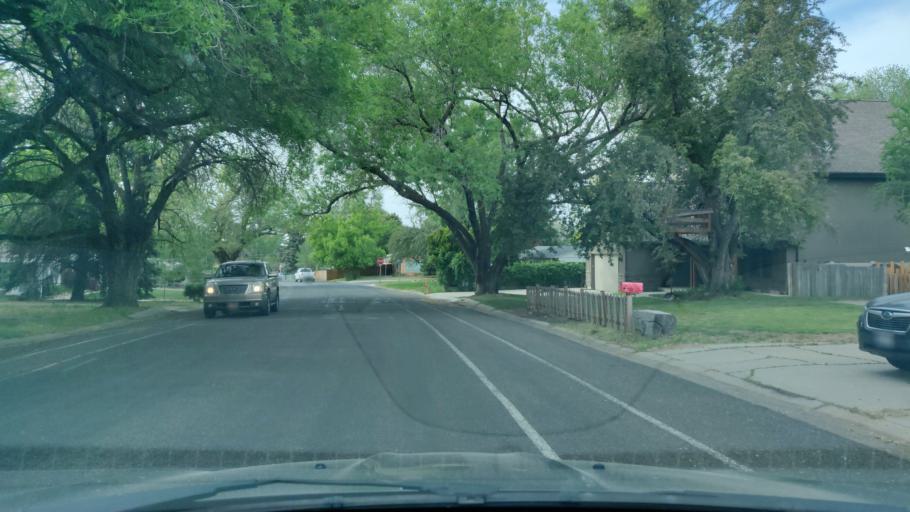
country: US
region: Utah
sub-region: Salt Lake County
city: Little Cottonwood Creek Valley
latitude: 40.6270
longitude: -111.8371
